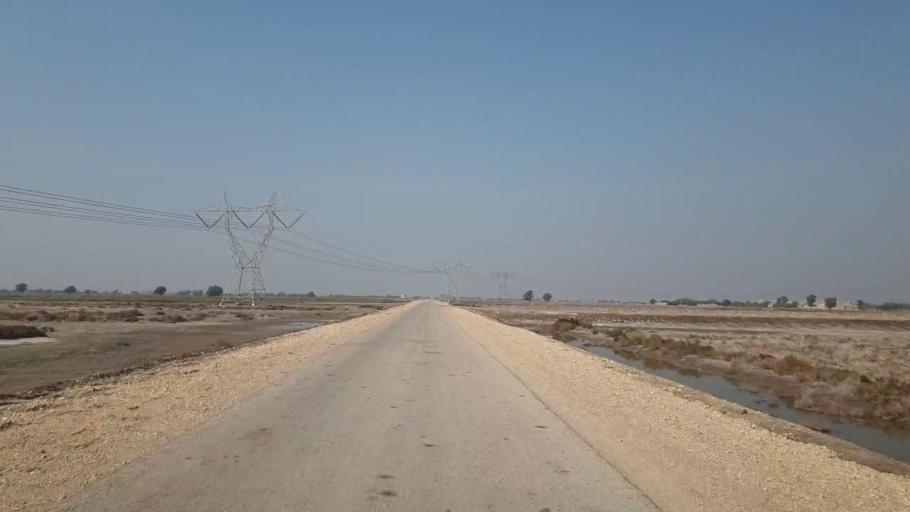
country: PK
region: Sindh
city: Sehwan
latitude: 26.4275
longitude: 67.7714
